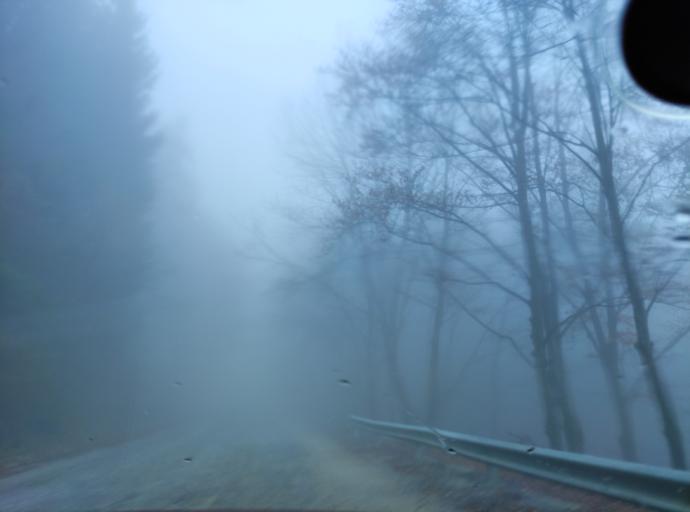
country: BG
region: Sofia-Capital
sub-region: Stolichna Obshtina
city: Sofia
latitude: 42.6147
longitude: 23.2951
